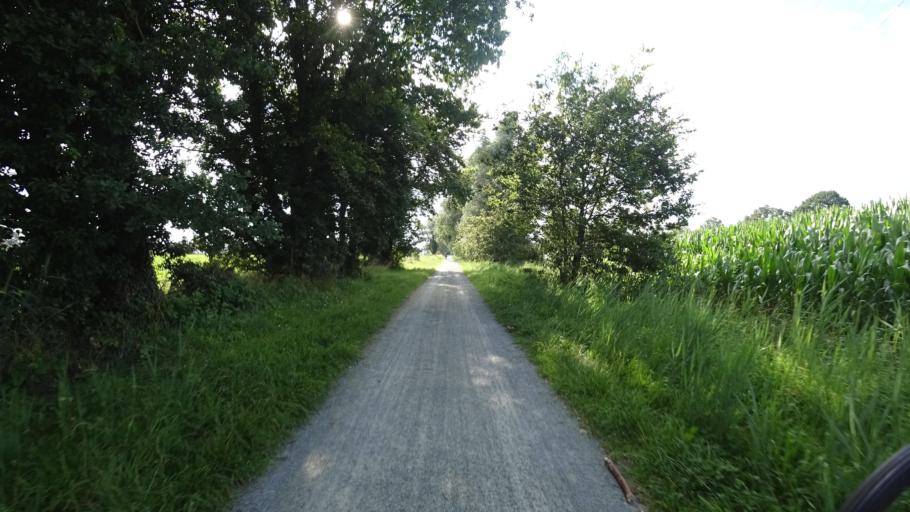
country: BE
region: Flanders
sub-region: Provincie West-Vlaanderen
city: Beernem
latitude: 51.2053
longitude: 3.3491
